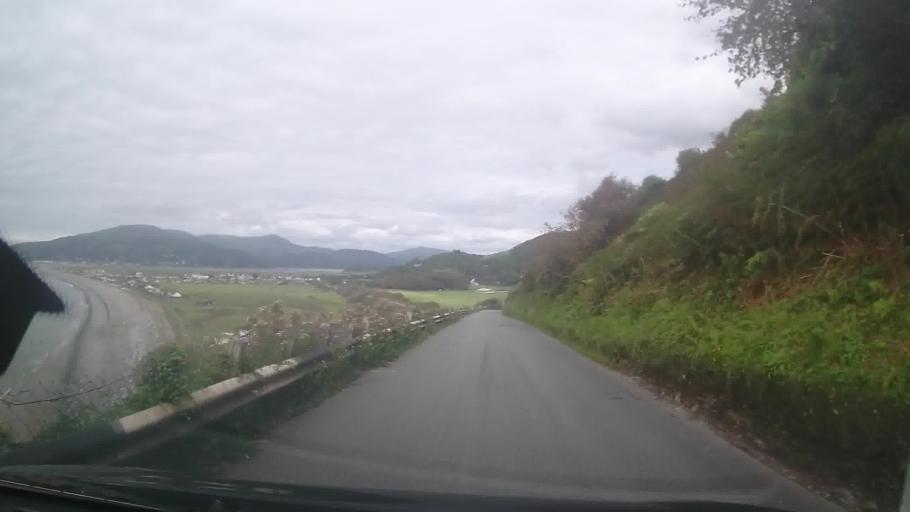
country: GB
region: Wales
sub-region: Gwynedd
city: Barmouth
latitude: 52.6871
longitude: -4.0567
